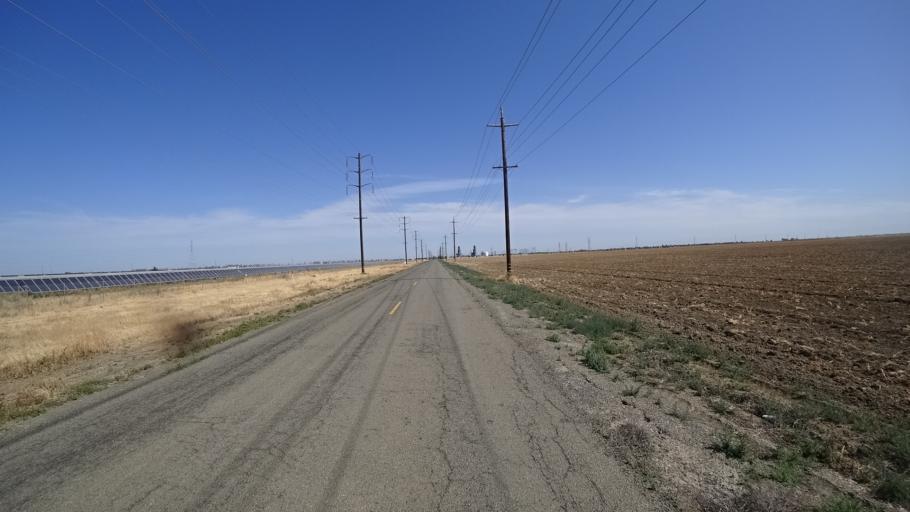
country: US
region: California
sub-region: Kings County
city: Lemoore Station
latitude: 36.2324
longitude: -119.9052
